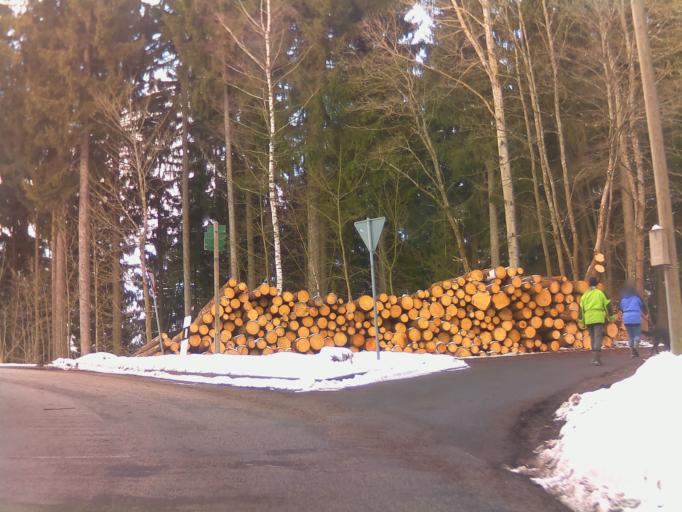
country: DE
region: Thuringia
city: Benshausen
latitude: 50.6267
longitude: 10.6229
